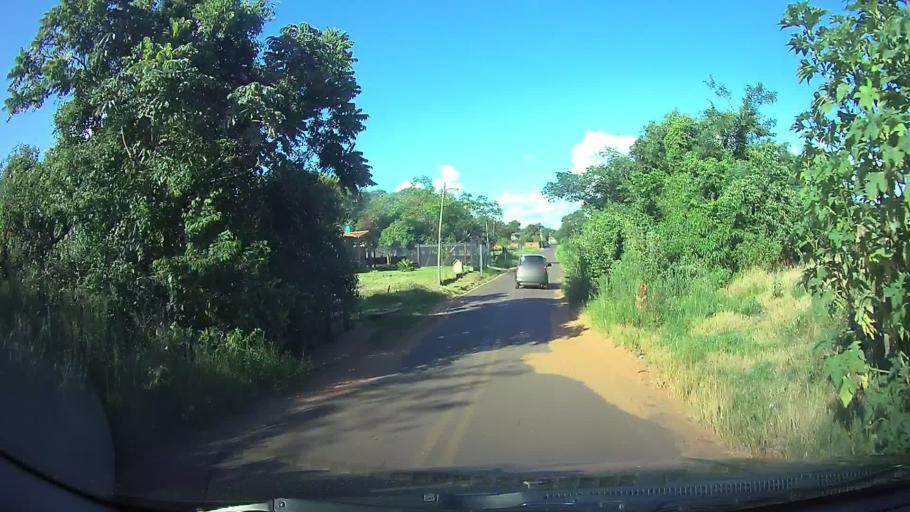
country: PY
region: Central
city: Aregua
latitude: -25.3425
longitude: -57.3875
